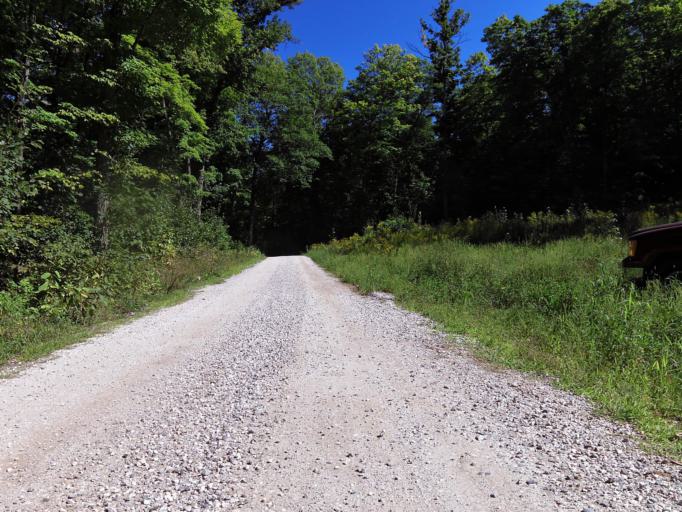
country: CA
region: Ontario
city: Renfrew
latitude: 45.1307
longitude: -76.6957
